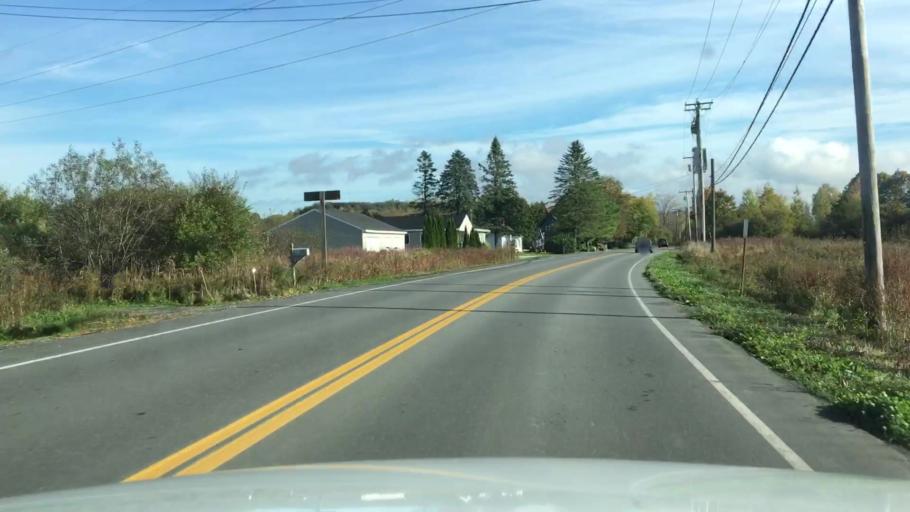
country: US
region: Maine
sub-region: Knox County
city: Thomaston
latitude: 44.0867
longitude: -69.1664
